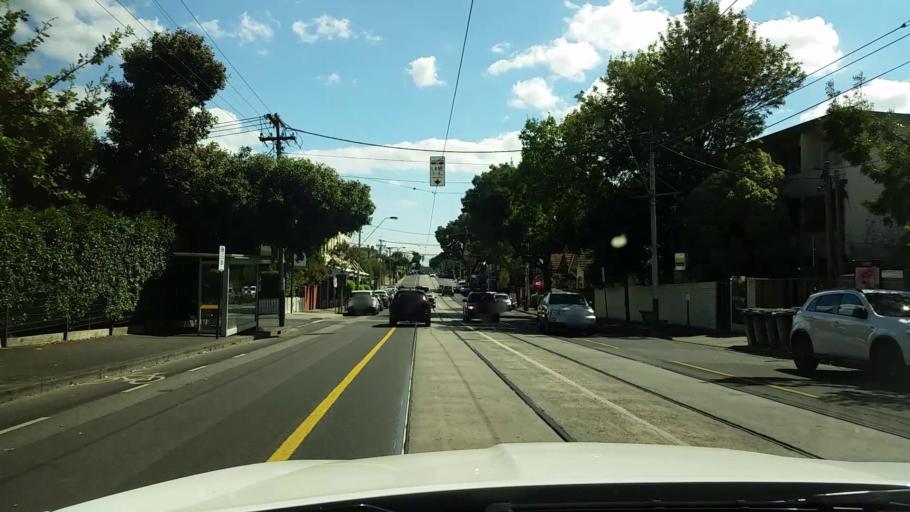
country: AU
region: Victoria
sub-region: Stonnington
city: Toorak
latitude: -37.8540
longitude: 145.0090
